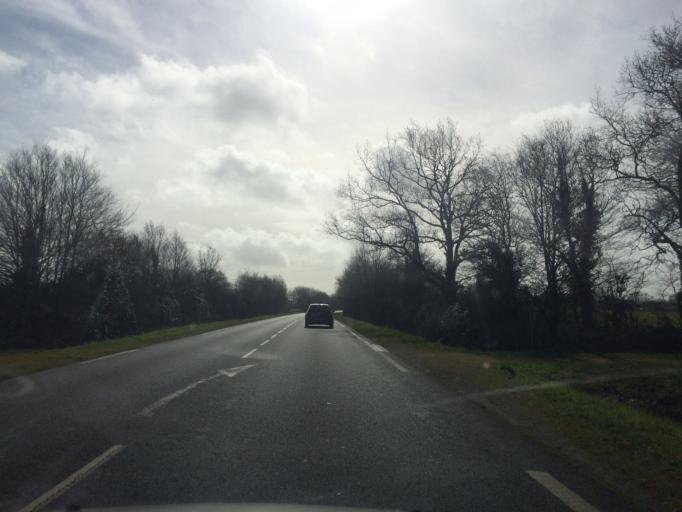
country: FR
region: Pays de la Loire
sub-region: Departement de la Loire-Atlantique
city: Besne
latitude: 47.3856
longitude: -2.0965
